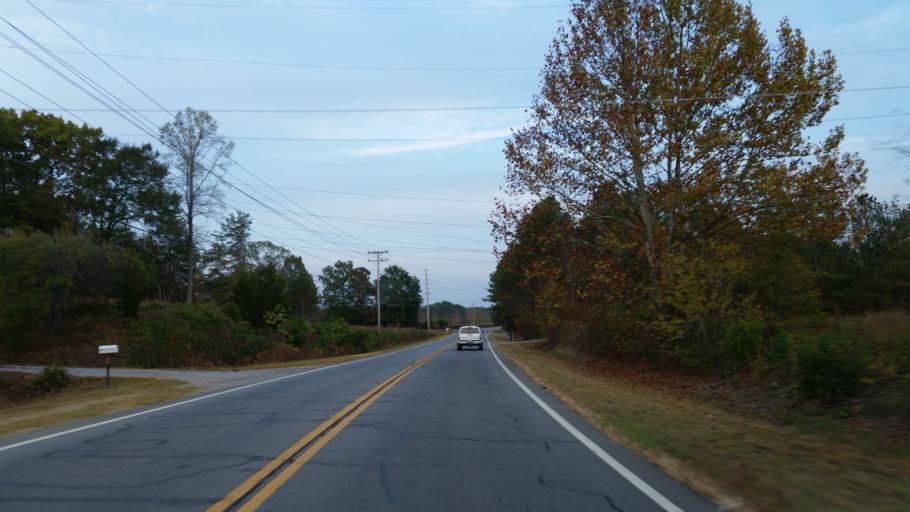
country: US
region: Georgia
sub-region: Gordon County
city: Calhoun
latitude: 34.6000
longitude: -84.9266
